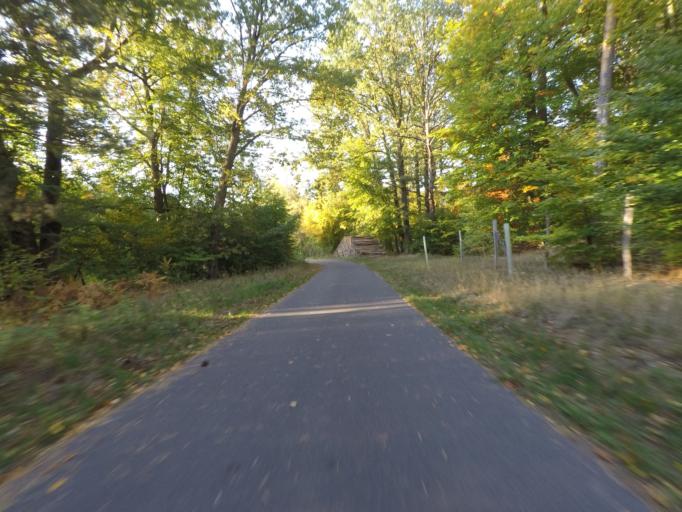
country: DE
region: Brandenburg
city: Biesenthal
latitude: 52.7932
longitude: 13.6297
